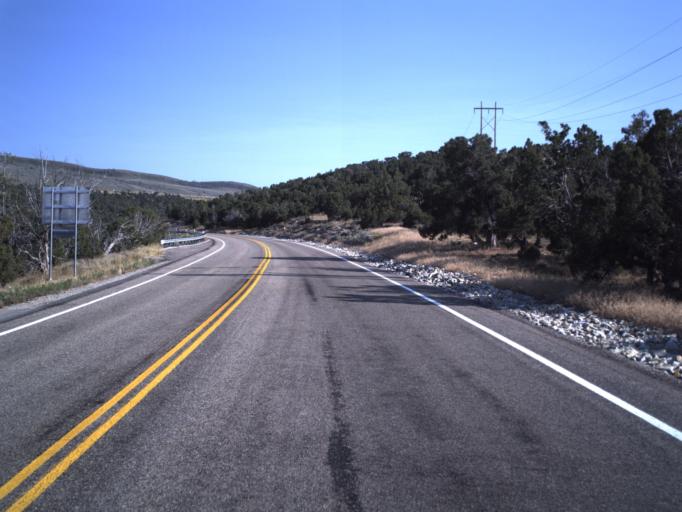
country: US
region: Utah
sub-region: Uintah County
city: Vernal
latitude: 40.6372
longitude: -109.4797
